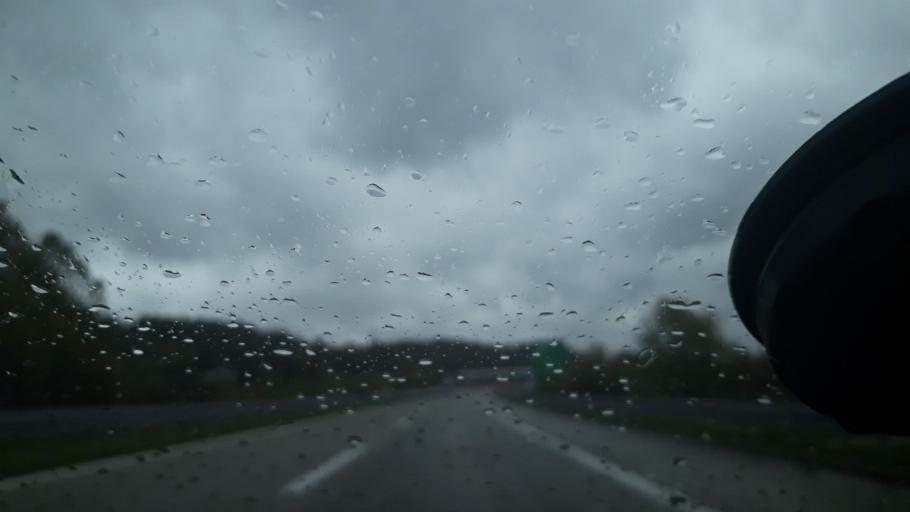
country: BA
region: Republika Srpska
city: Laktasi
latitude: 44.8886
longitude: 17.2840
